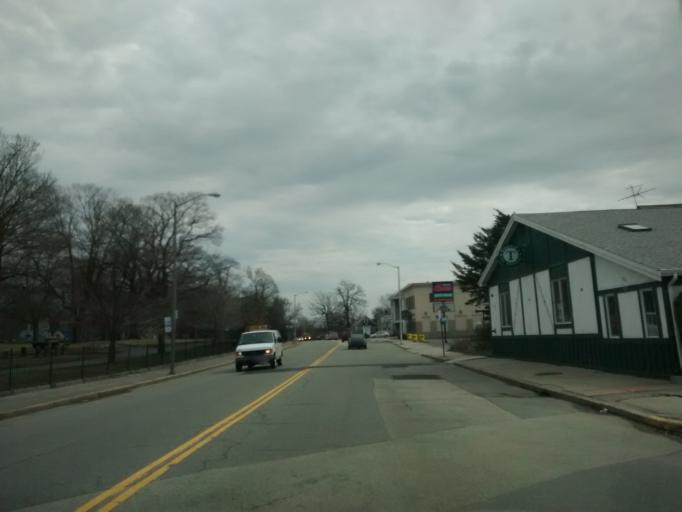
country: US
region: Massachusetts
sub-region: Worcester County
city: Worcester
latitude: 42.2810
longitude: -71.8056
